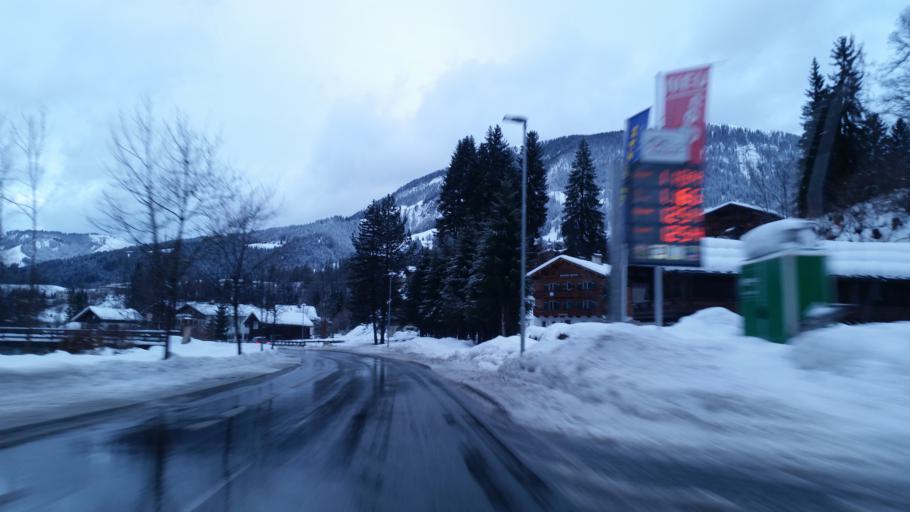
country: AT
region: Tyrol
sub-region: Politischer Bezirk Kitzbuhel
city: Fieberbrunn
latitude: 47.4840
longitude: 12.5346
